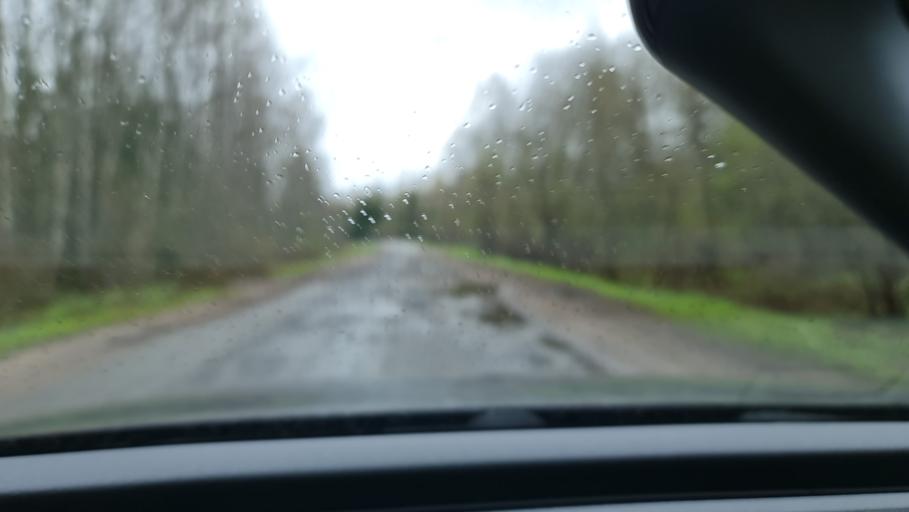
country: RU
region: Novgorod
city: Marevo
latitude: 57.2622
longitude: 32.0704
